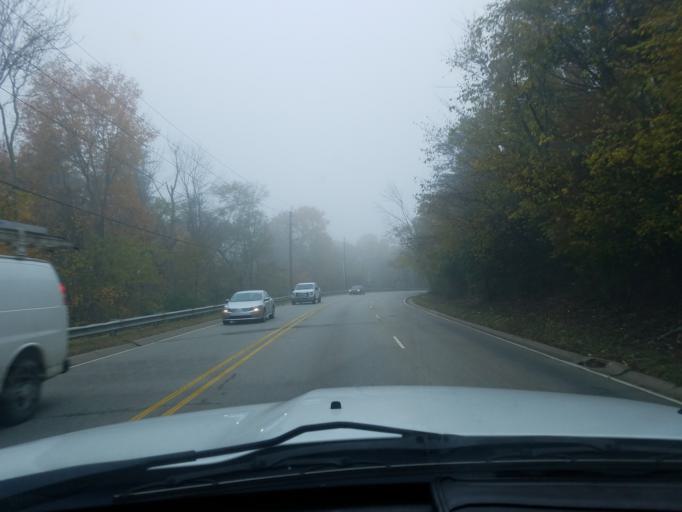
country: US
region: Indiana
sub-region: Floyd County
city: New Albany
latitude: 38.3125
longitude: -85.8489
